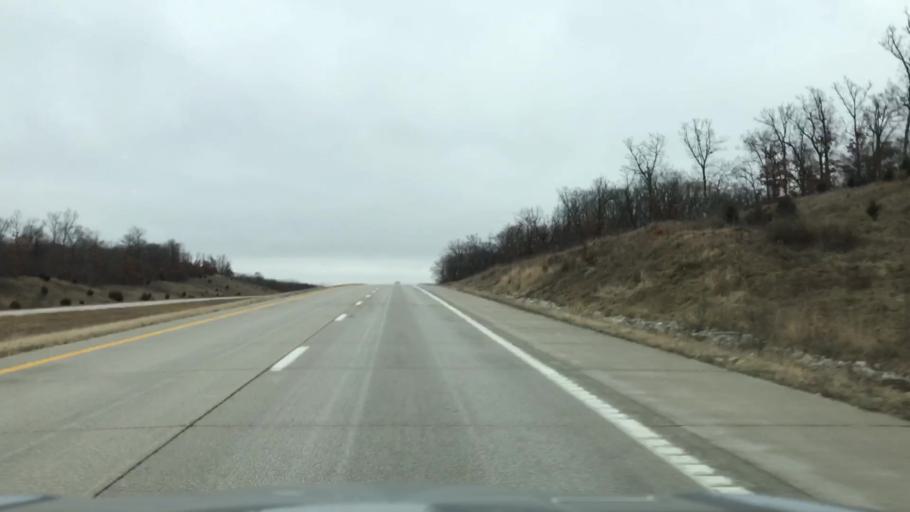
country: US
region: Missouri
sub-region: Linn County
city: Marceline
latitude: 39.7590
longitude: -92.8507
